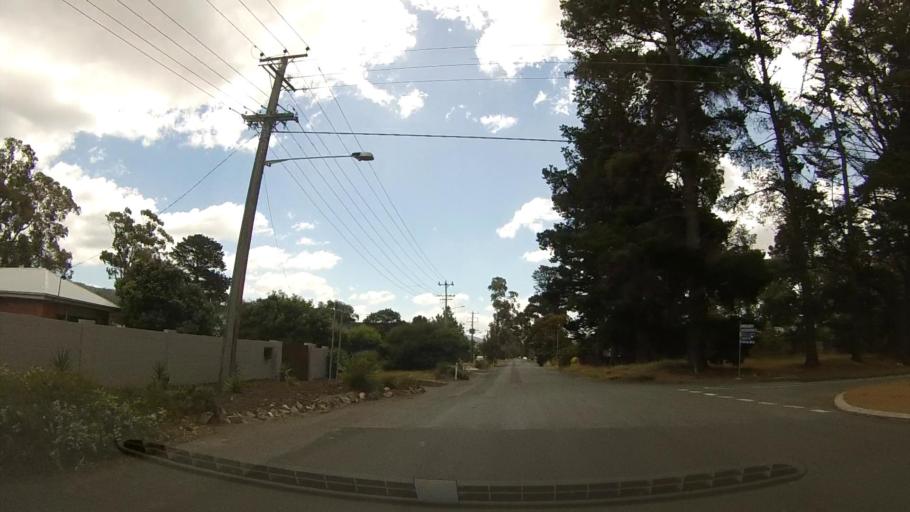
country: AU
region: Tasmania
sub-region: Clarence
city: Seven Mile Beach
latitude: -42.8614
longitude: 147.5050
